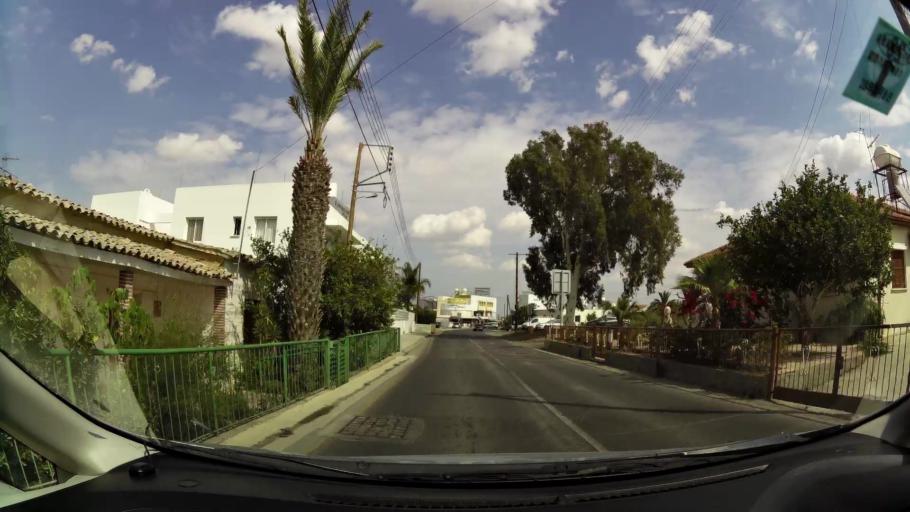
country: CY
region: Lefkosia
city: Tseri
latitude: 35.0762
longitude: 33.3224
